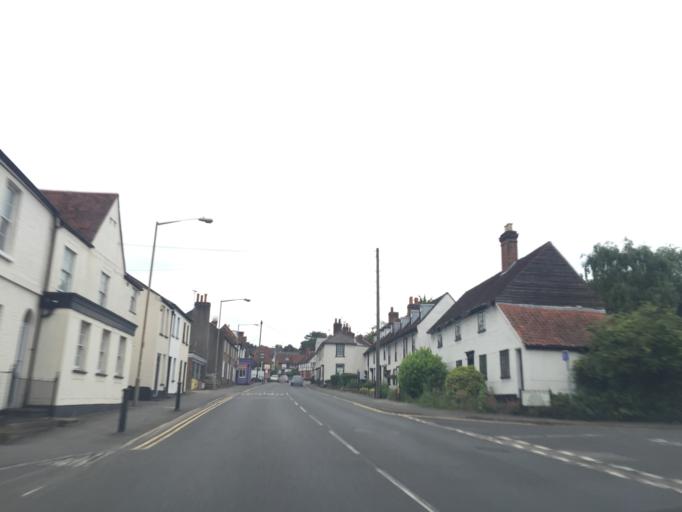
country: GB
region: England
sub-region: Essex
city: Chipping Ongar
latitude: 51.7020
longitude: 0.2439
